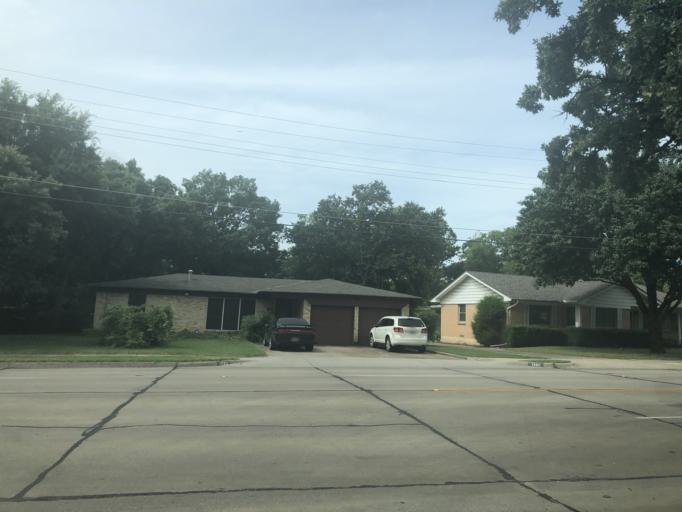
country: US
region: Texas
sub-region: Dallas County
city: Irving
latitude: 32.8094
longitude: -96.9645
